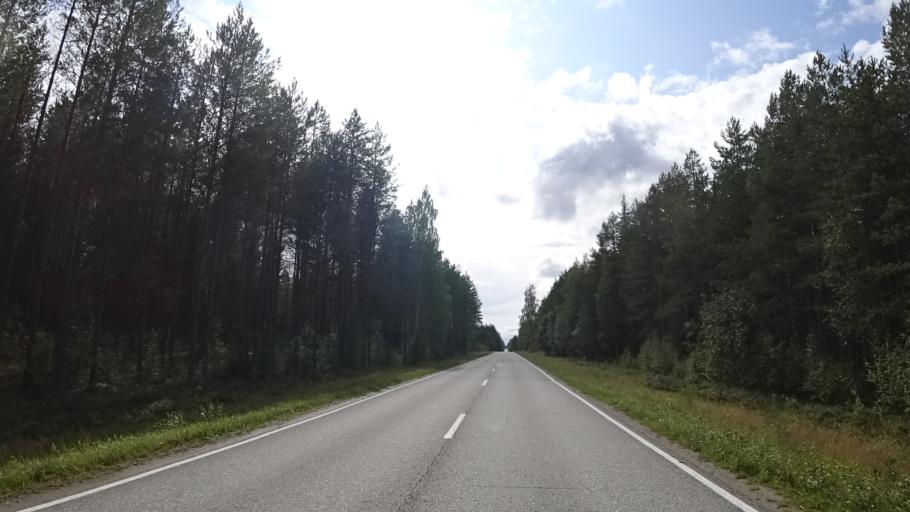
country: FI
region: North Karelia
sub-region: Joensuu
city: Ilomantsi
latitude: 62.7619
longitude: 31.0207
